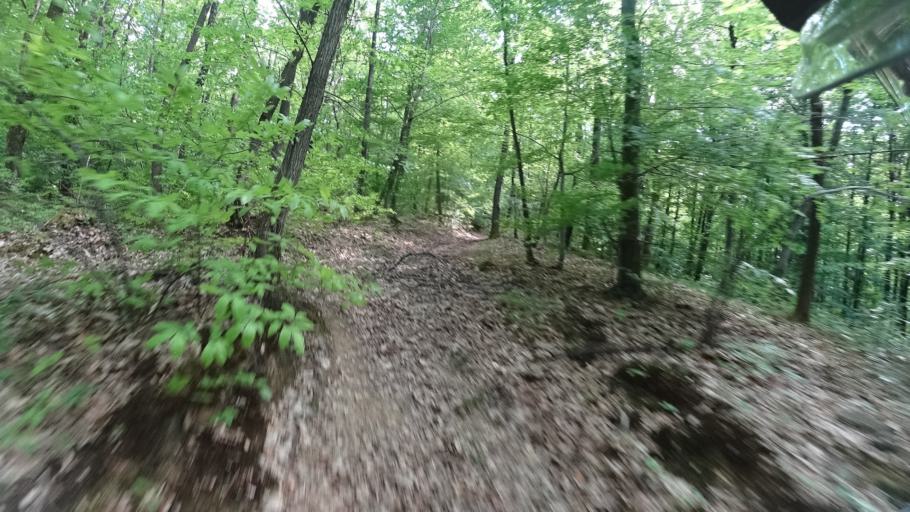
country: HR
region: Grad Zagreb
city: Kasina
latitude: 45.9382
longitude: 15.9414
